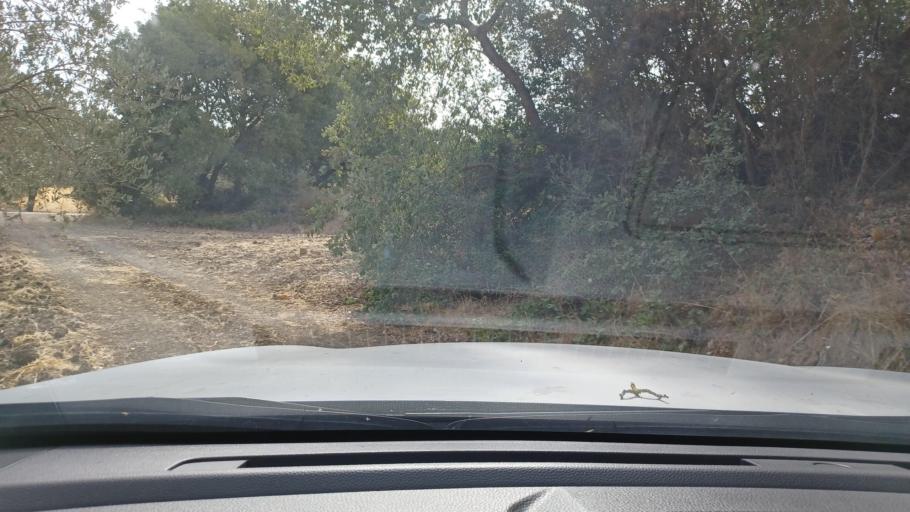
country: CY
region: Pafos
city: Polis
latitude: 35.0091
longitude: 32.5156
